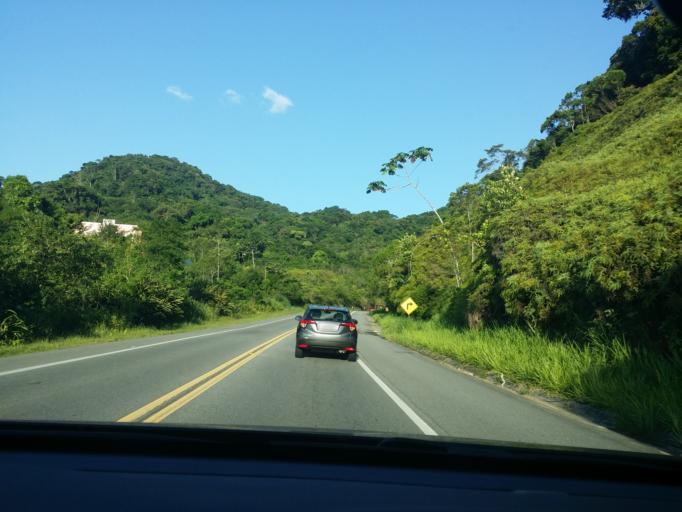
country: BR
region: Sao Paulo
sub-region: Sao Sebastiao
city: Sao Sebastiao
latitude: -23.7427
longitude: -45.7332
